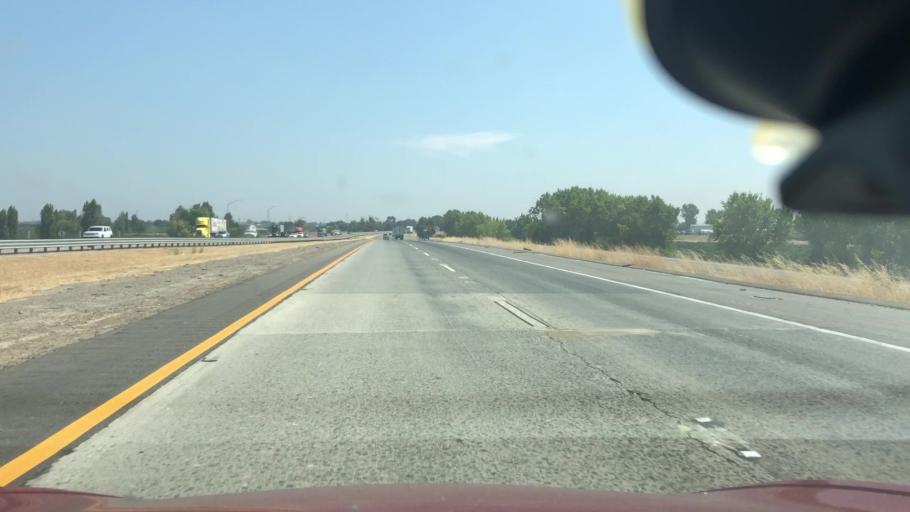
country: US
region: California
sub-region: San Joaquin County
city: Thornton
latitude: 38.1889
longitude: -121.4046
